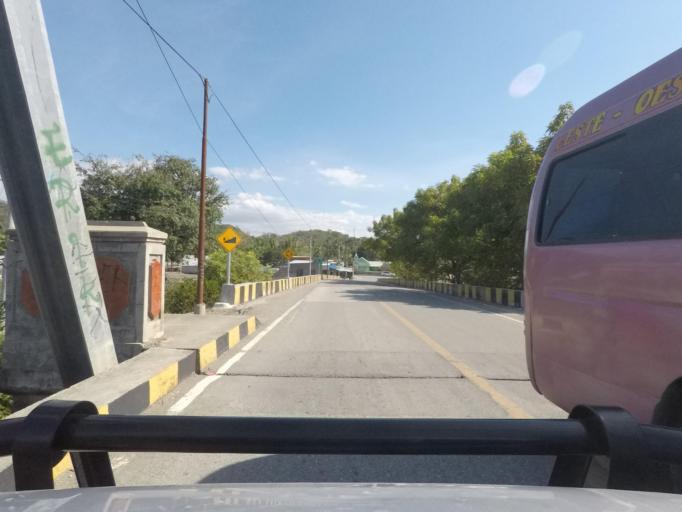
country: ID
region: East Nusa Tenggara
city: Atambua
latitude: -8.9461
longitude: 124.9740
